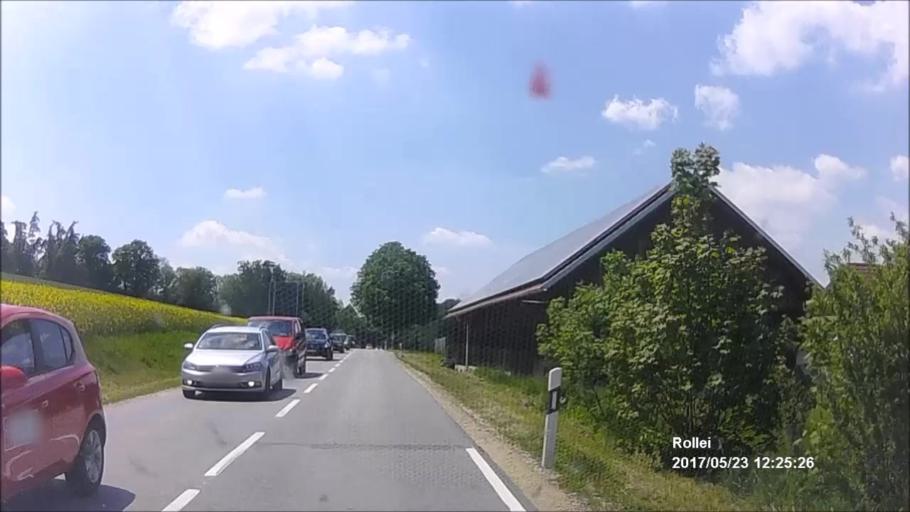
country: DE
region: Bavaria
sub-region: Lower Bavaria
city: Buch
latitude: 48.6700
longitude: 12.1856
